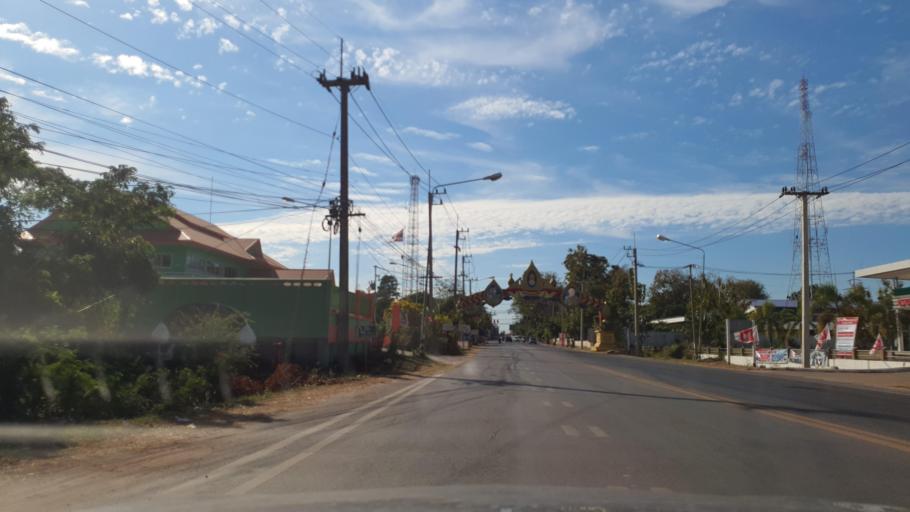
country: TH
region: Kalasin
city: Kuchinarai
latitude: 16.5378
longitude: 104.0574
